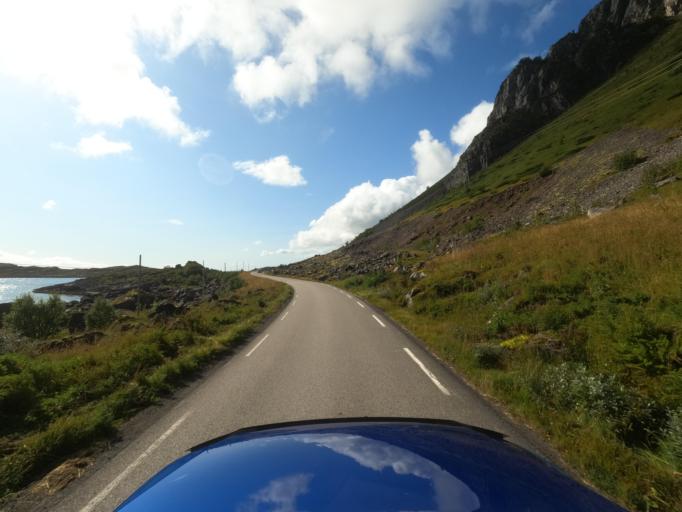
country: NO
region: Nordland
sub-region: Vestvagoy
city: Evjen
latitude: 68.1938
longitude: 14.0266
